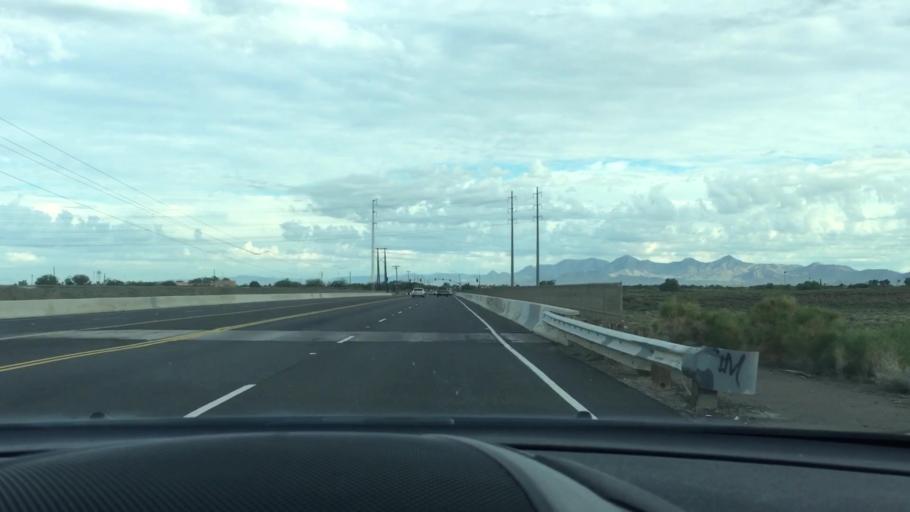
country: US
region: Arizona
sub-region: Maricopa County
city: Mesa
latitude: 33.4521
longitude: -111.8573
